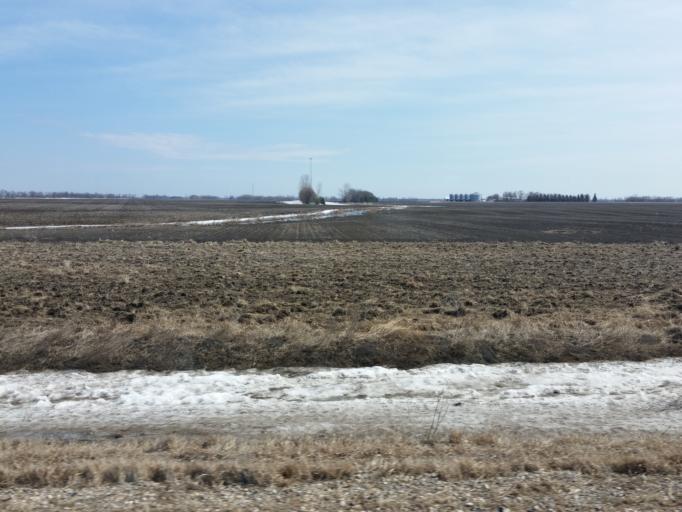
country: US
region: North Dakota
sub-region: Walsh County
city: Grafton
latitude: 48.2991
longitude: -97.2548
